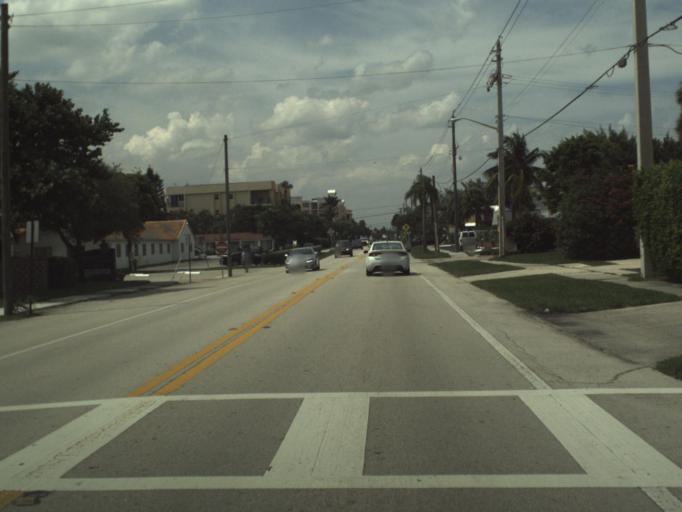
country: US
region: Florida
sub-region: Broward County
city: Hillsboro Beach
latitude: 26.3094
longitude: -80.0777
